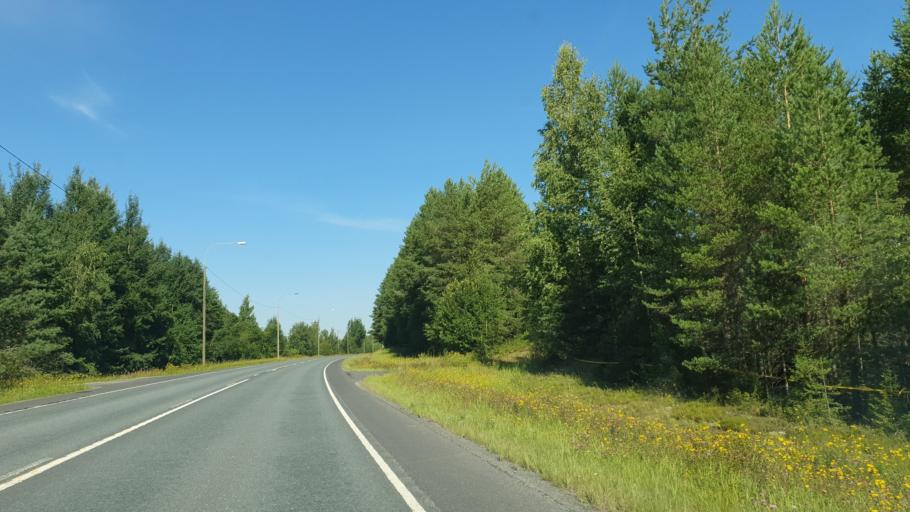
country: FI
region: Northern Savo
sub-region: Kuopio
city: Siilinjaervi
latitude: 63.1648
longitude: 27.5647
